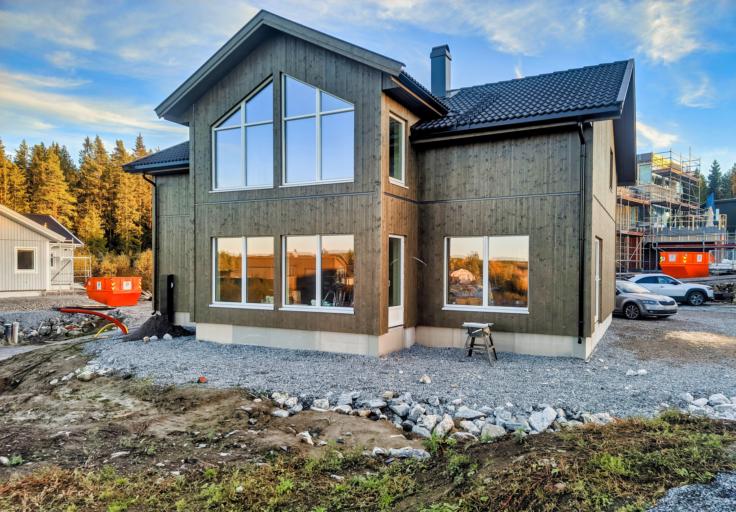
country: NO
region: Ostfold
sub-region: Sarpsborg
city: Sarpsborg
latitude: 59.3433
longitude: 11.1821
